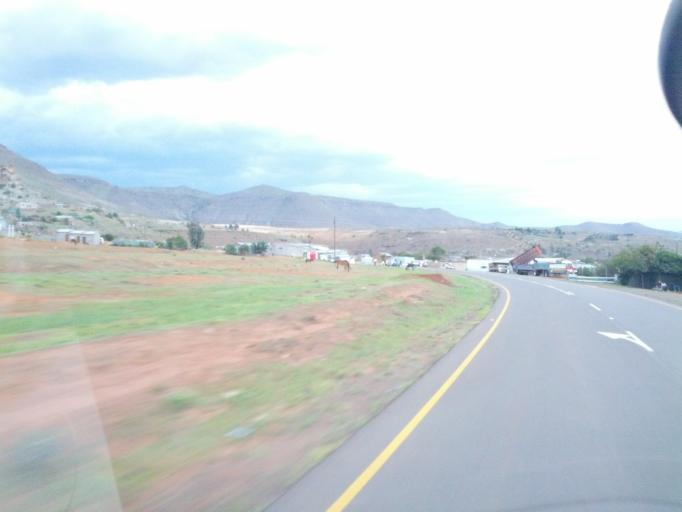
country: LS
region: Qacha's Nek
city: Qacha's Nek
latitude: -30.0471
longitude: 28.3639
